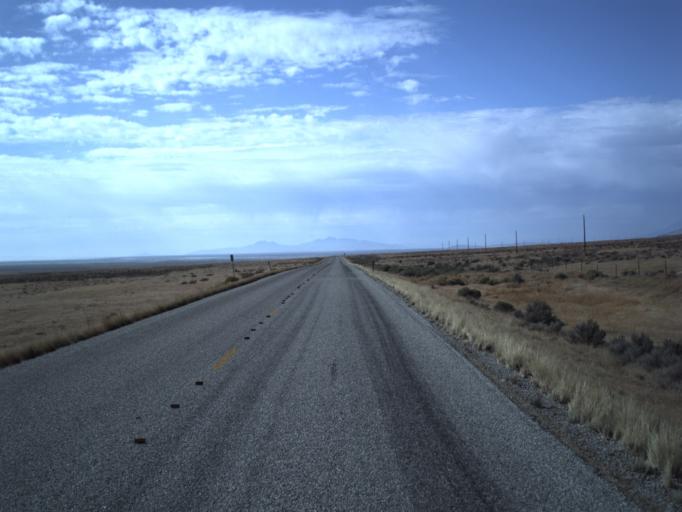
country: US
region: Utah
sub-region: Tooele County
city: Wendover
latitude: 41.5126
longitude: -113.6002
